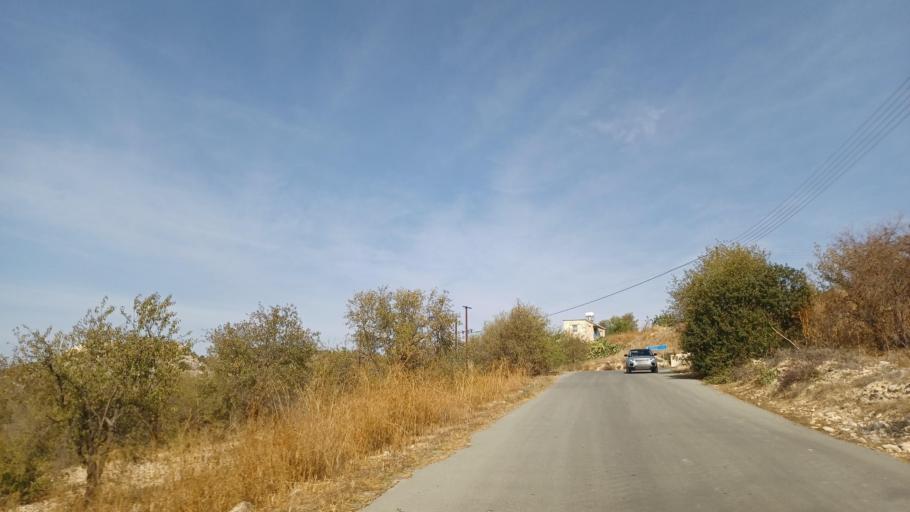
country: CY
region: Pafos
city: Polis
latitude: 34.9722
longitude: 32.5038
